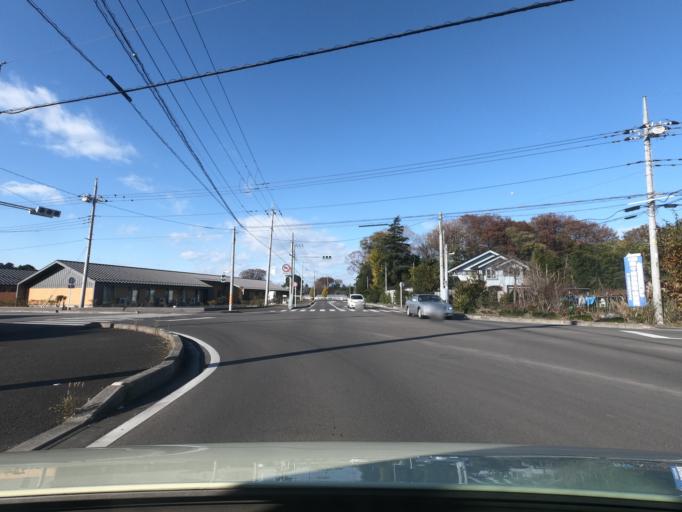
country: JP
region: Tochigi
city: Oyama
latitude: 36.2343
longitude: 139.7695
